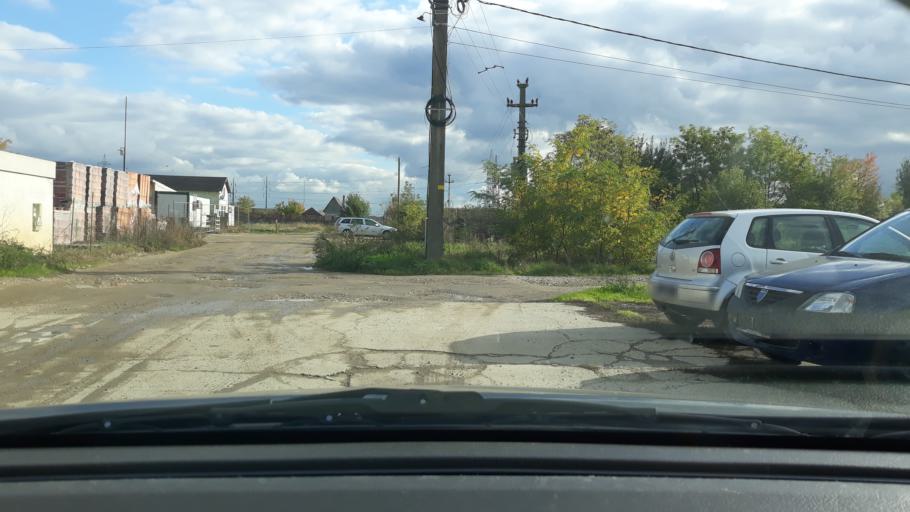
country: RO
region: Bihor
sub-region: Comuna Sanmartin
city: Sanmartin
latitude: 47.0260
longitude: 21.9492
